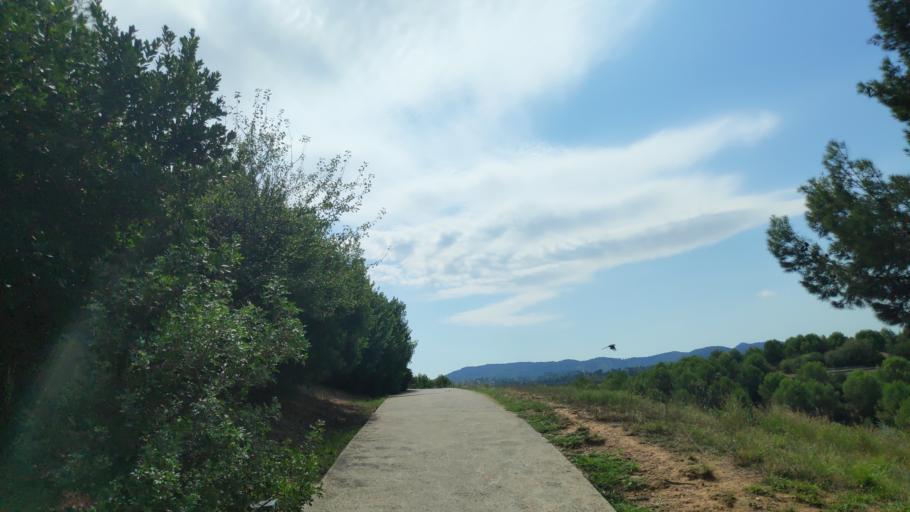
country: ES
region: Catalonia
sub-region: Provincia de Barcelona
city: Sant Cugat del Valles
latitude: 41.4760
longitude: 2.0627
